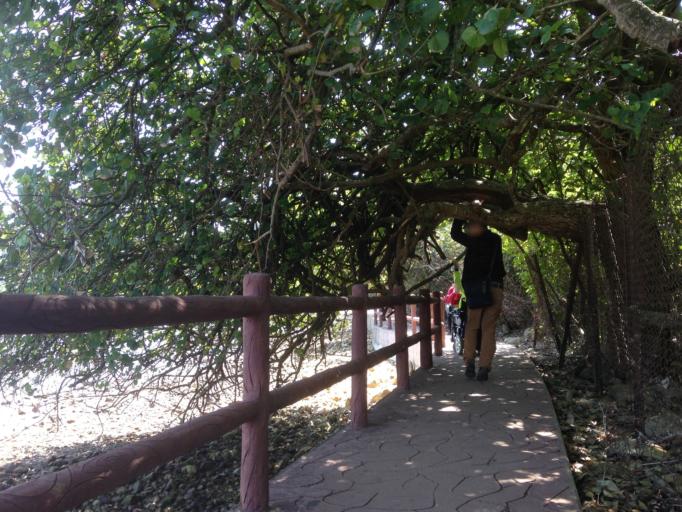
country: HK
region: Sai Kung
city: Sai Kung
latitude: 22.4324
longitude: 114.2556
